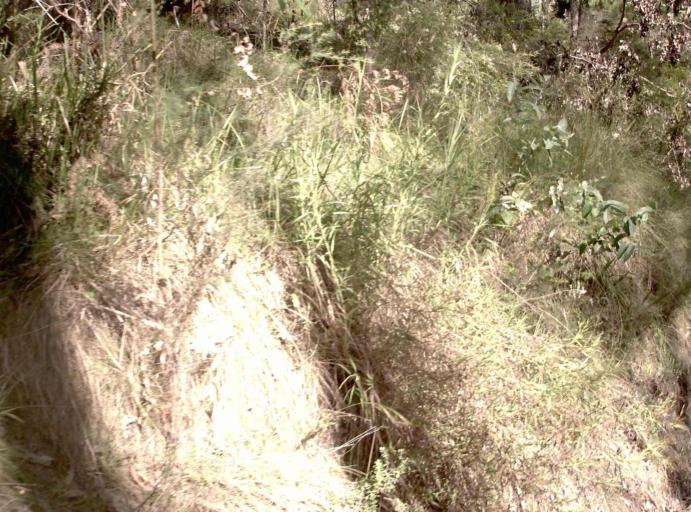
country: AU
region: New South Wales
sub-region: Bombala
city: Bombala
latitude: -37.3829
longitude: 148.6260
